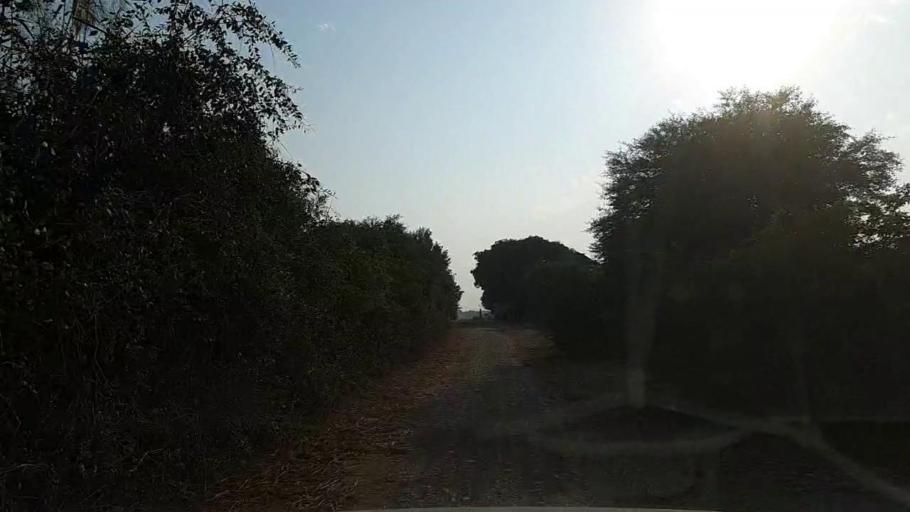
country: PK
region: Sindh
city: Mirpur Batoro
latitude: 24.7843
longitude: 68.2461
